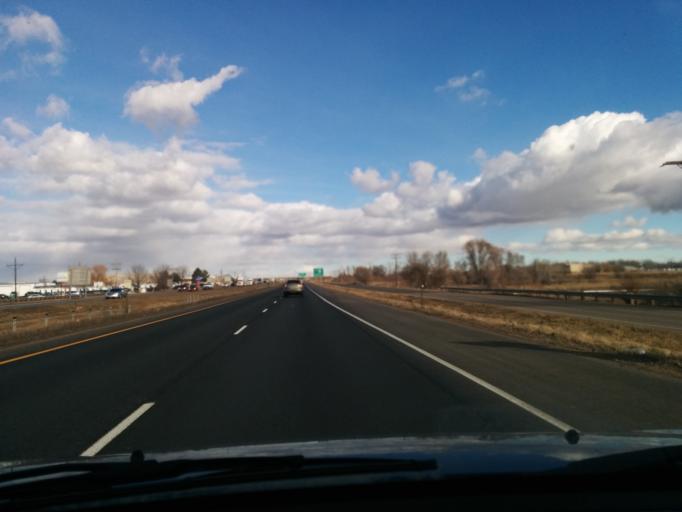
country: US
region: Colorado
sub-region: Larimer County
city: Fort Collins
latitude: 40.5725
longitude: -105.0012
